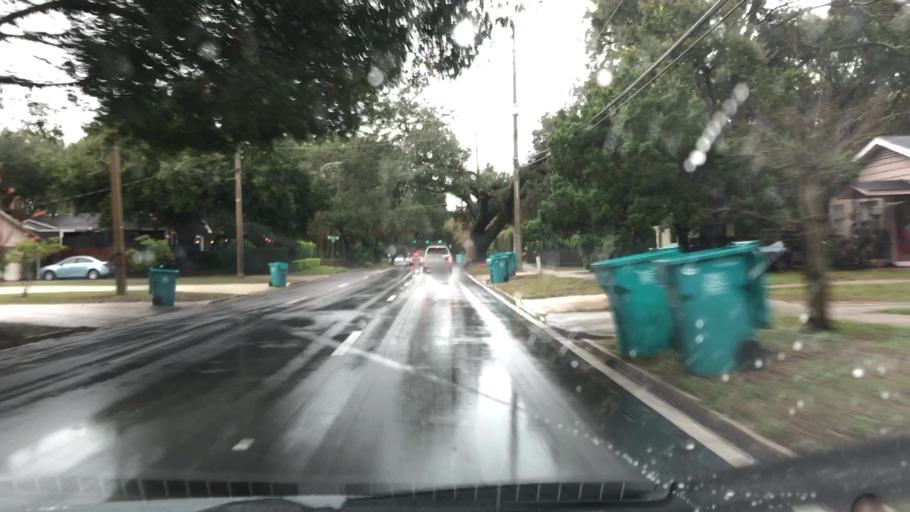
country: US
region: Florida
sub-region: Orange County
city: Orlando
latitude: 28.5385
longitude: -81.3665
